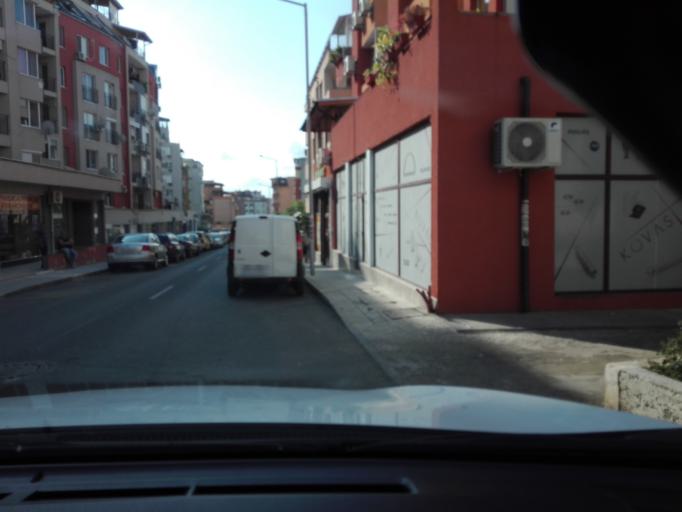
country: BG
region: Burgas
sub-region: Obshtina Burgas
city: Burgas
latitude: 42.4542
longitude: 27.4179
